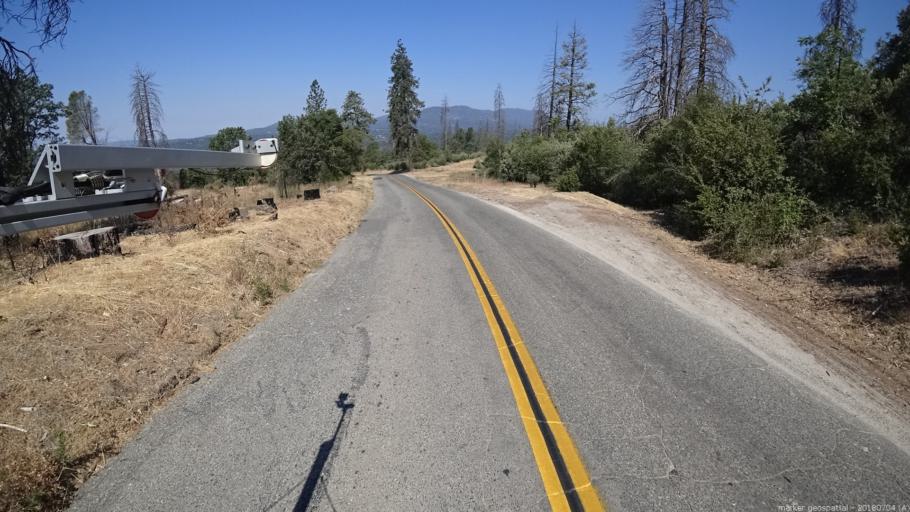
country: US
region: California
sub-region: Fresno County
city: Auberry
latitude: 37.2346
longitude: -119.4753
